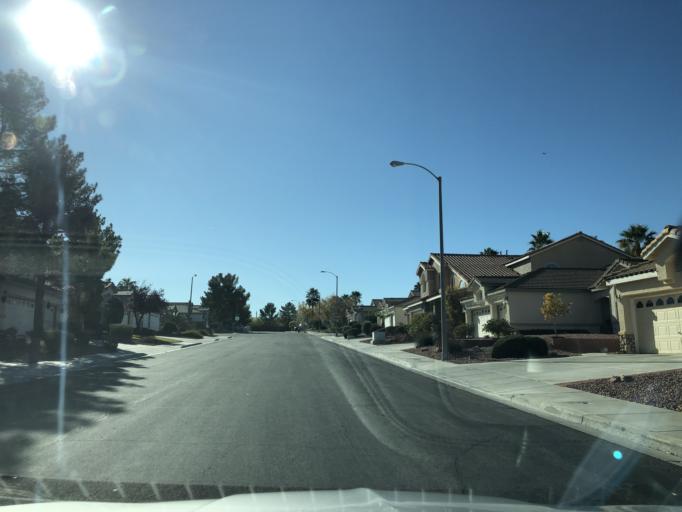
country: US
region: Nevada
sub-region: Clark County
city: Whitney
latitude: 36.0105
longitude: -115.0863
